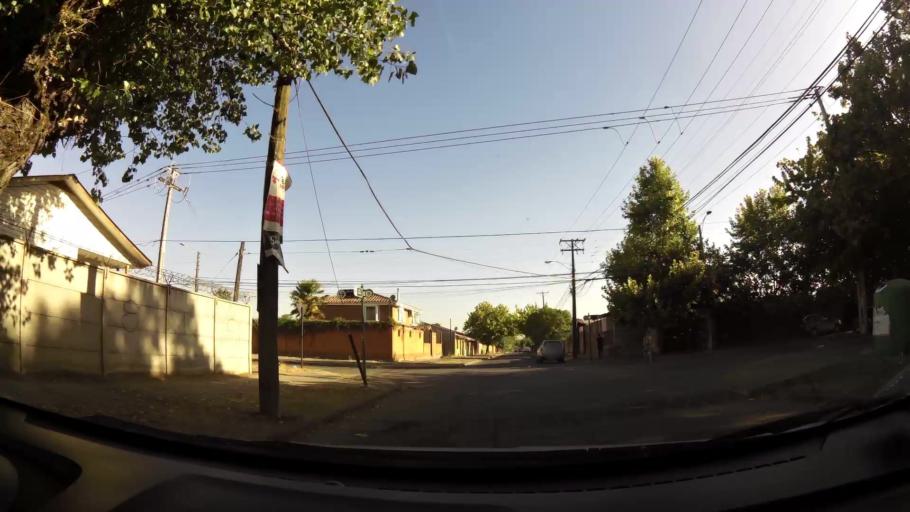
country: CL
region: Maule
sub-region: Provincia de Talca
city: Talca
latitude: -35.4349
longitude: -71.6542
